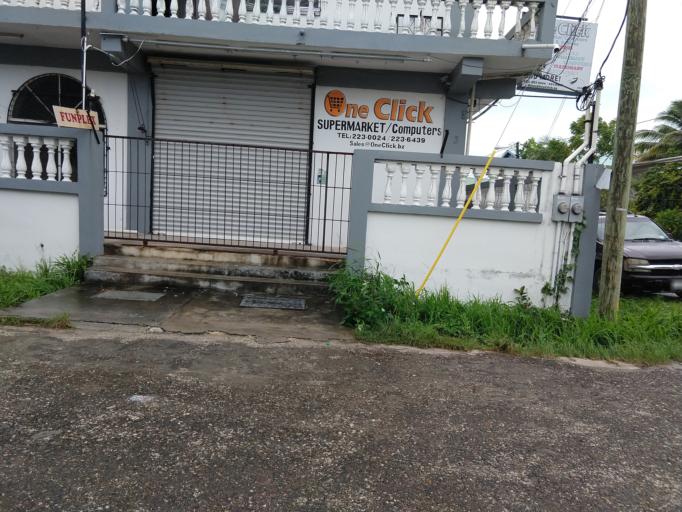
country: BZ
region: Belize
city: Belize City
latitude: 17.5063
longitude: -88.1920
